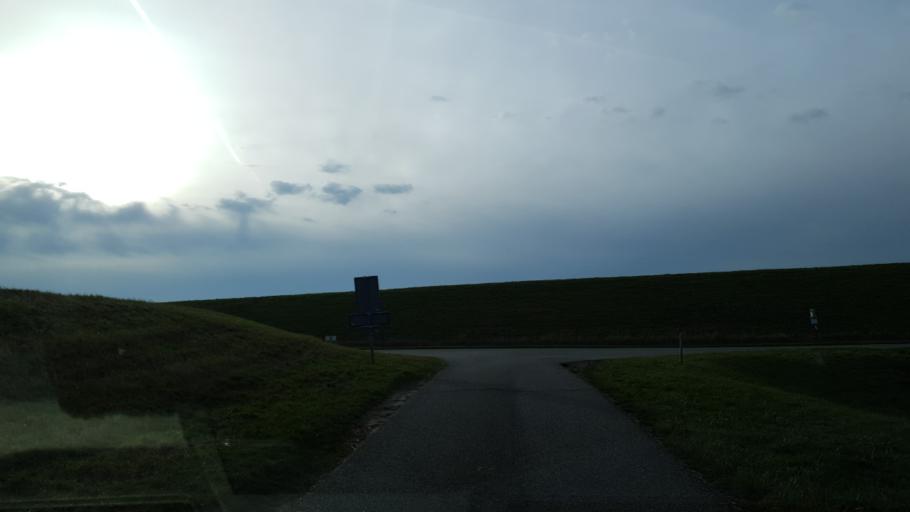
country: NL
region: North Brabant
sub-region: Gemeente Woensdrecht
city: Woensdrecht
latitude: 51.3929
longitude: 4.2359
